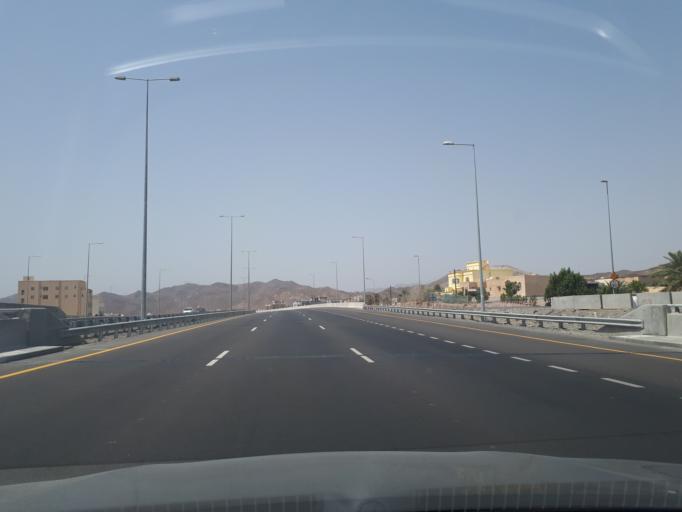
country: OM
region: Muhafazat ad Dakhiliyah
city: Bidbid
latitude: 23.4079
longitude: 58.0997
